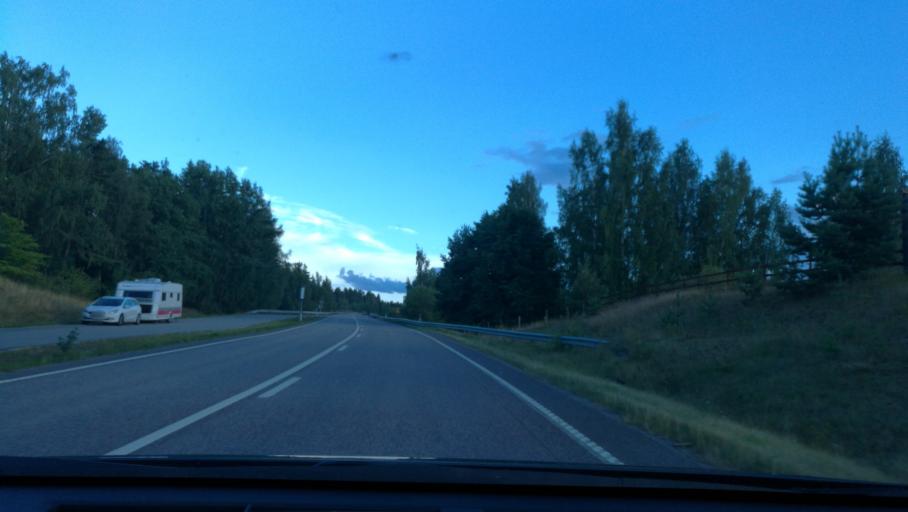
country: SE
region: Vaestmanland
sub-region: Kungsors Kommun
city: Kungsoer
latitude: 59.2399
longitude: 16.1004
